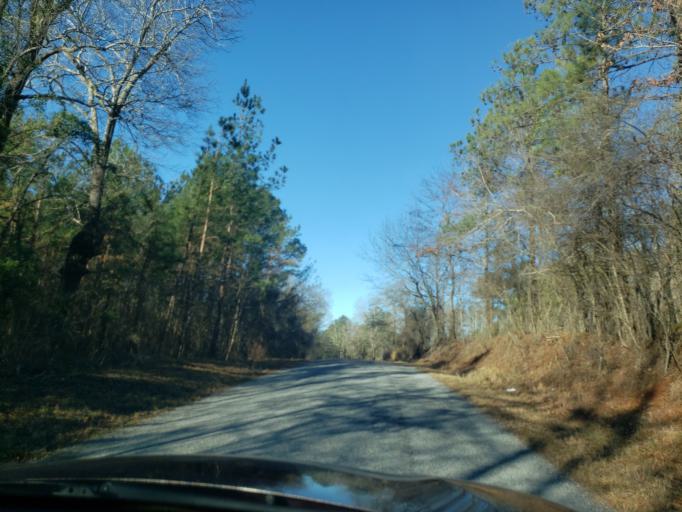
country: US
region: Alabama
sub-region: Elmore County
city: Tallassee
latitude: 32.6709
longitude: -85.8789
